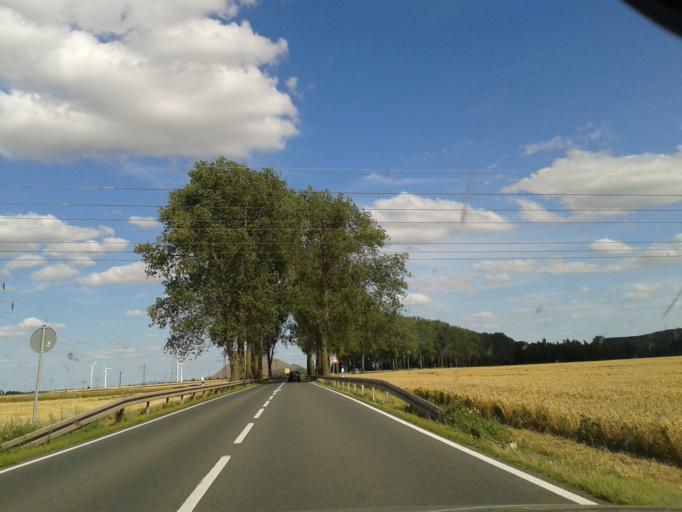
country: DE
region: Saxony-Anhalt
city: Klostermansfeld
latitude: 51.5856
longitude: 11.5190
